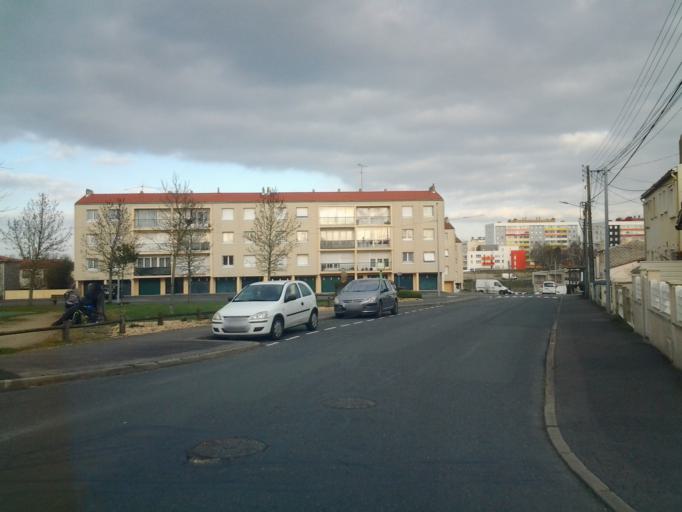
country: FR
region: Pays de la Loire
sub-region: Departement de la Vendee
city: La Roche-sur-Yon
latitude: 46.6795
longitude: -1.4444
